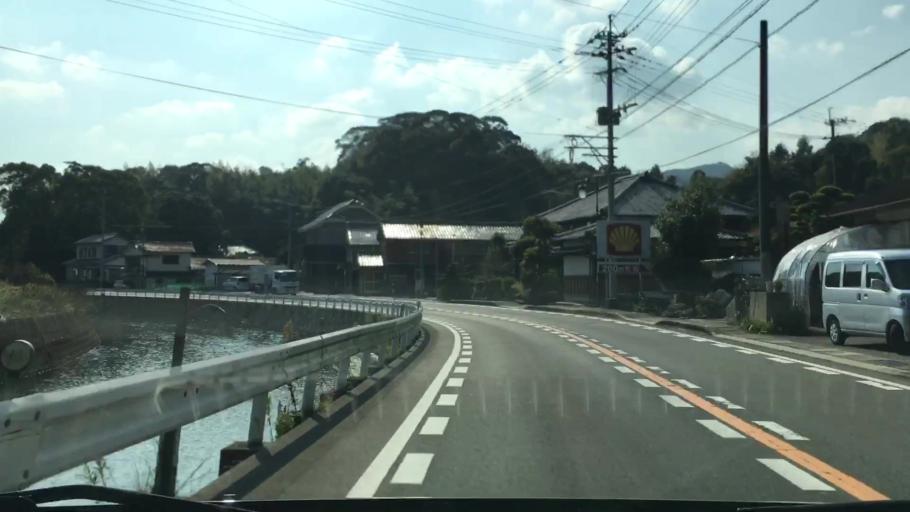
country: JP
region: Nagasaki
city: Togitsu
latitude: 32.9522
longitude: 129.7851
